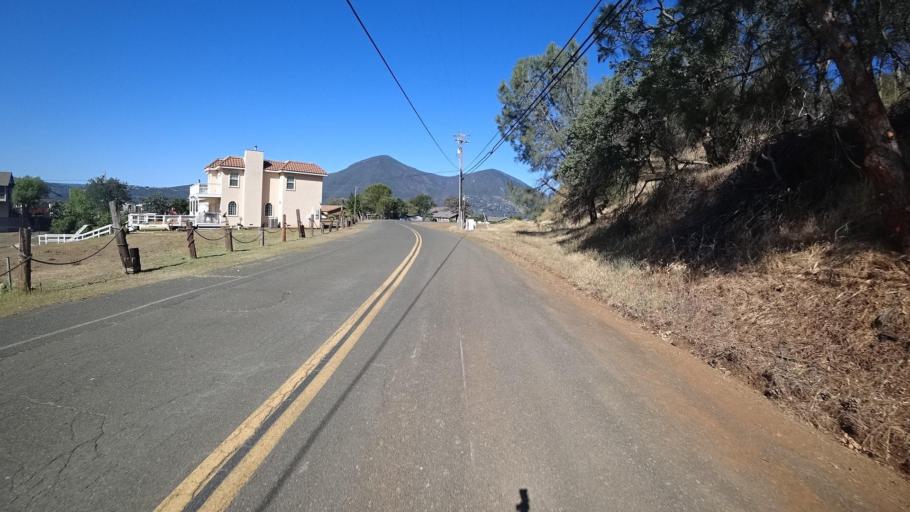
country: US
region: California
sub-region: Lake County
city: Clearlake Oaks
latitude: 38.9924
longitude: -122.7018
